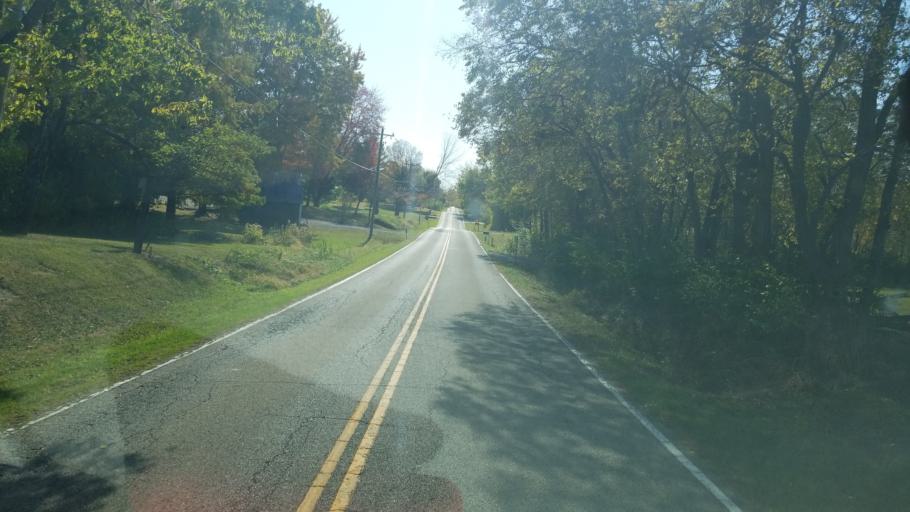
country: US
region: Ohio
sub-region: Warren County
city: Morrow
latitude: 39.4156
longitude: -84.0798
